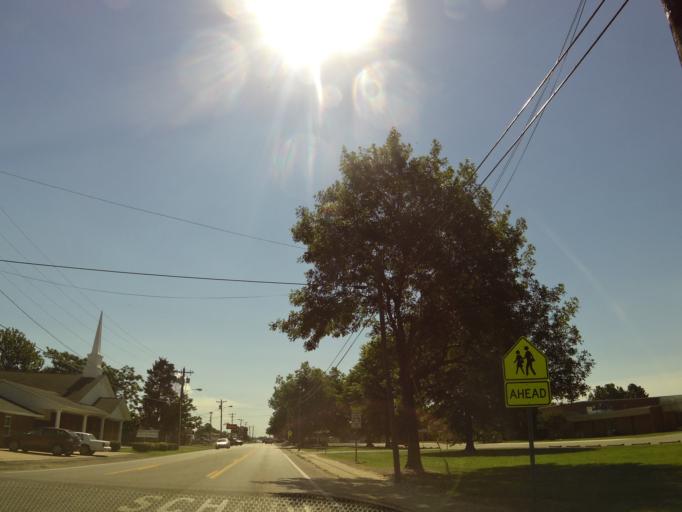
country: US
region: Arkansas
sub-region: Clay County
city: Piggott
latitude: 36.3819
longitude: -90.1809
